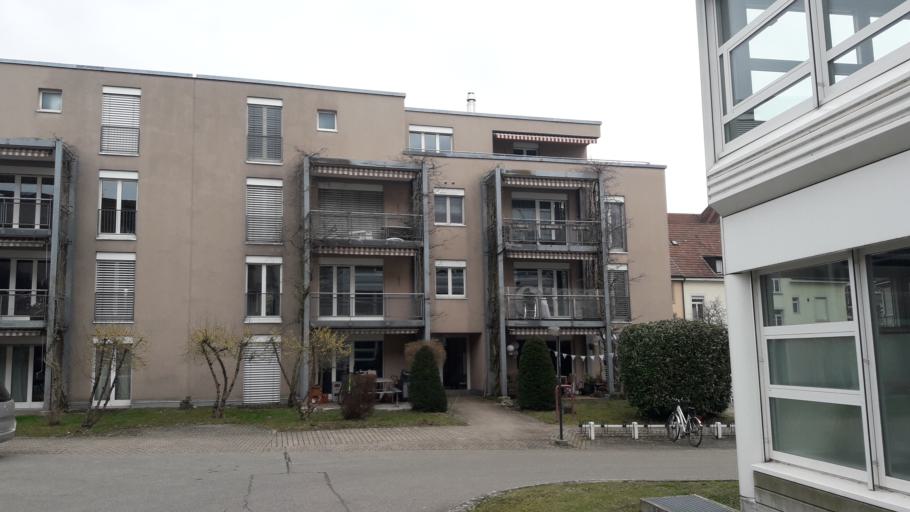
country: CH
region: Solothurn
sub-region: Bezirk Solothurn
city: Solothurn
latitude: 47.2105
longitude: 7.5303
